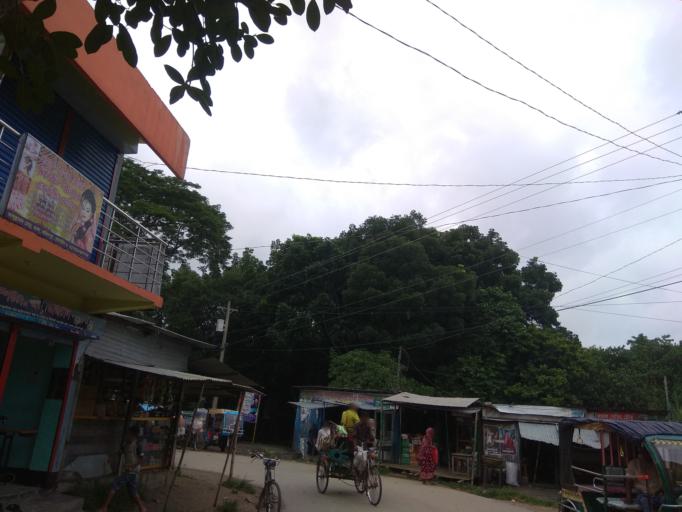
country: BD
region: Dhaka
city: Dohar
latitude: 23.4249
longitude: 90.0632
